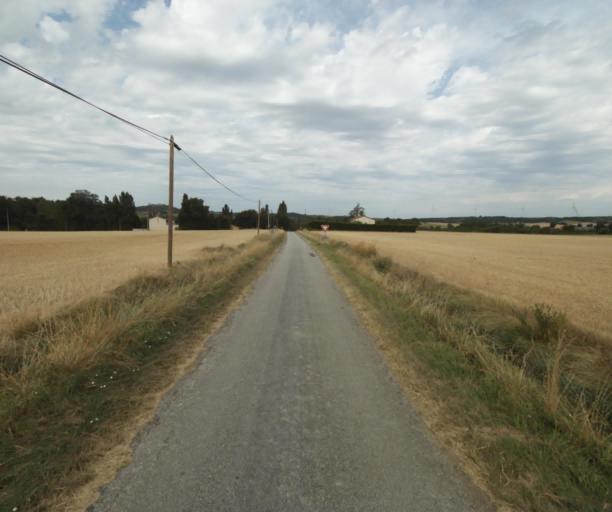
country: FR
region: Midi-Pyrenees
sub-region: Departement de la Haute-Garonne
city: Saint-Felix-Lauragais
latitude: 43.4405
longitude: 1.9294
